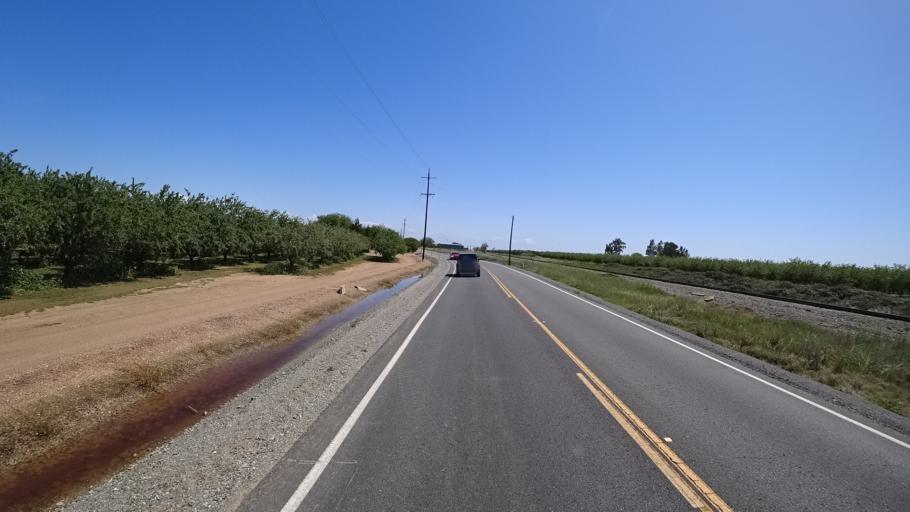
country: US
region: California
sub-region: Glenn County
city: Hamilton City
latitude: 39.7667
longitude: -122.0951
